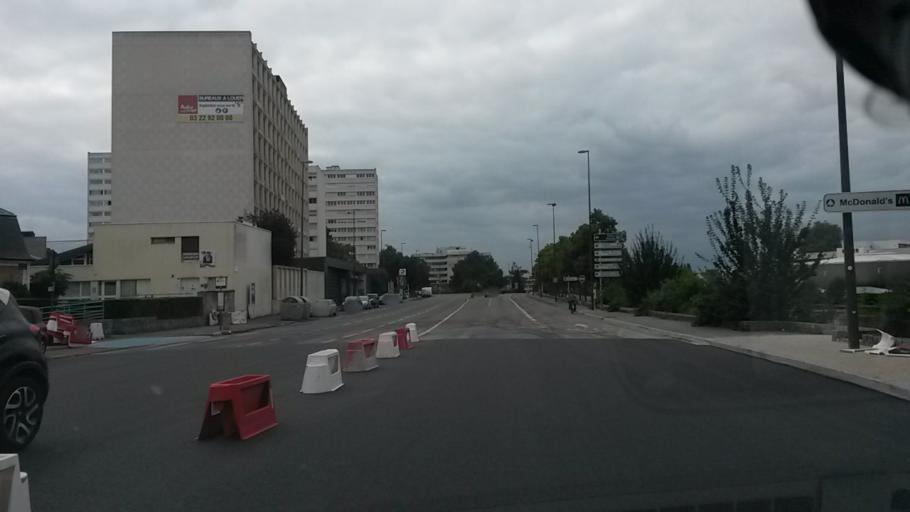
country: FR
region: Picardie
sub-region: Departement de la Somme
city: Amiens
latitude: 49.8982
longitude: 2.2943
